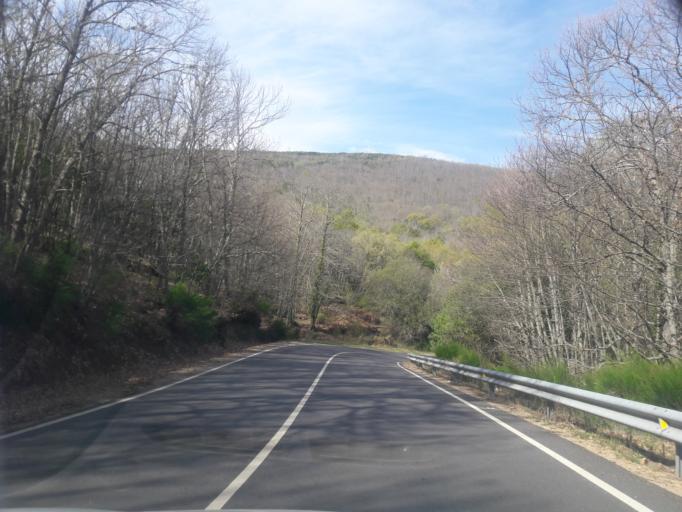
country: ES
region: Castille and Leon
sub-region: Provincia de Salamanca
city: Santibanez de la Sierra
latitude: 40.4890
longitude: -5.9213
